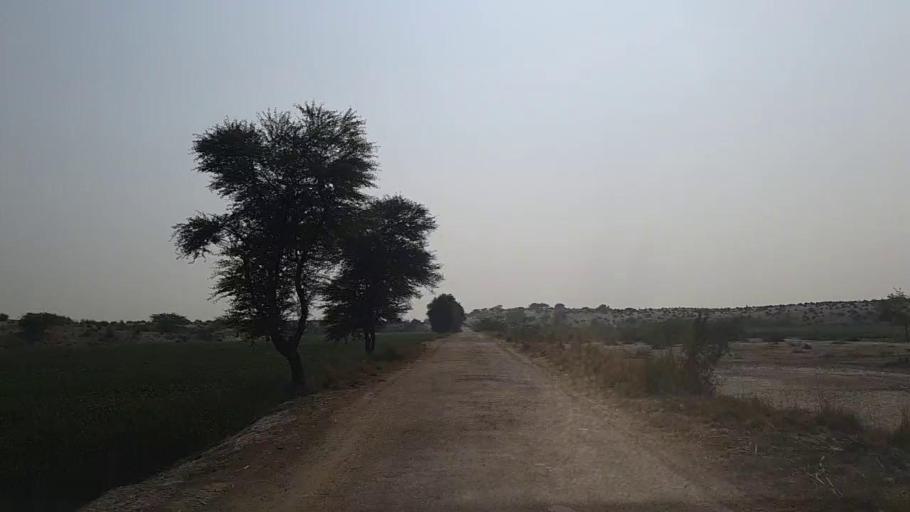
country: PK
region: Sindh
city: Jam Sahib
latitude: 26.4482
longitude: 68.5233
